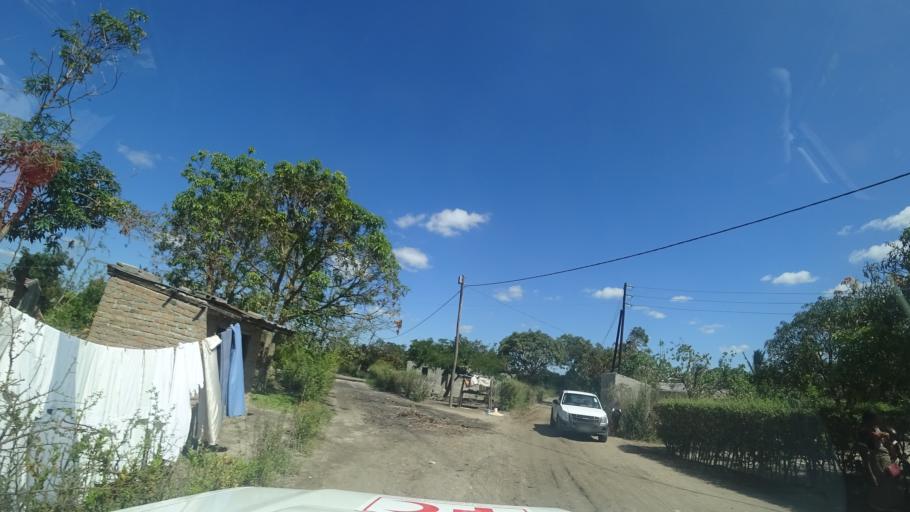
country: MZ
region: Sofala
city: Dondo
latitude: -19.4944
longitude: 34.5985
